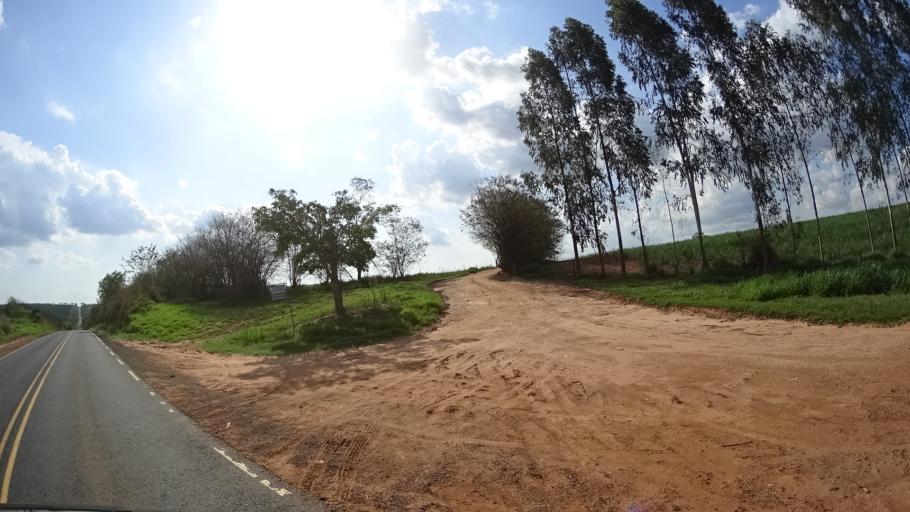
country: BR
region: Sao Paulo
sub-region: Urupes
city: Urupes
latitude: -21.2168
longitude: -49.3496
